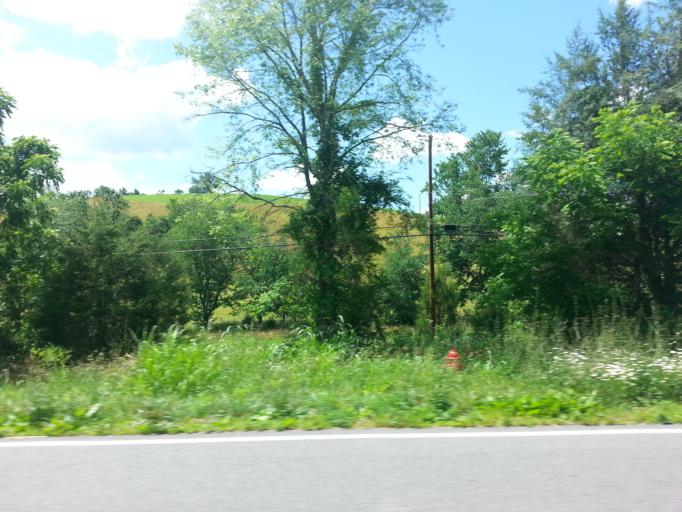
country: US
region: Virginia
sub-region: Lee County
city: Jonesville
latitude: 36.6914
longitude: -83.0924
